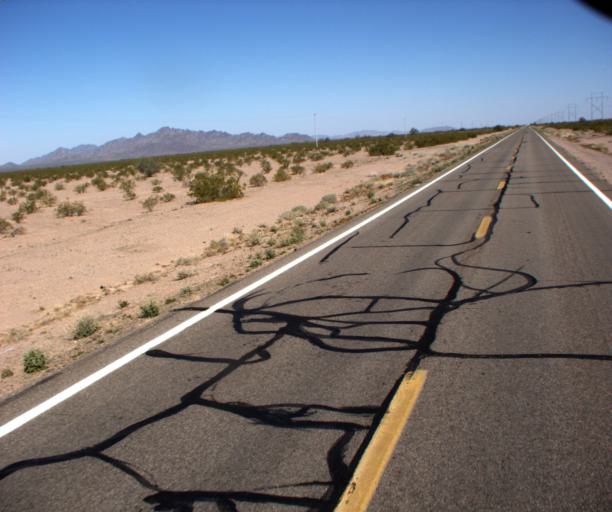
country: US
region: Arizona
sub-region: La Paz County
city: Quartzsite
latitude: 33.4202
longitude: -114.2170
